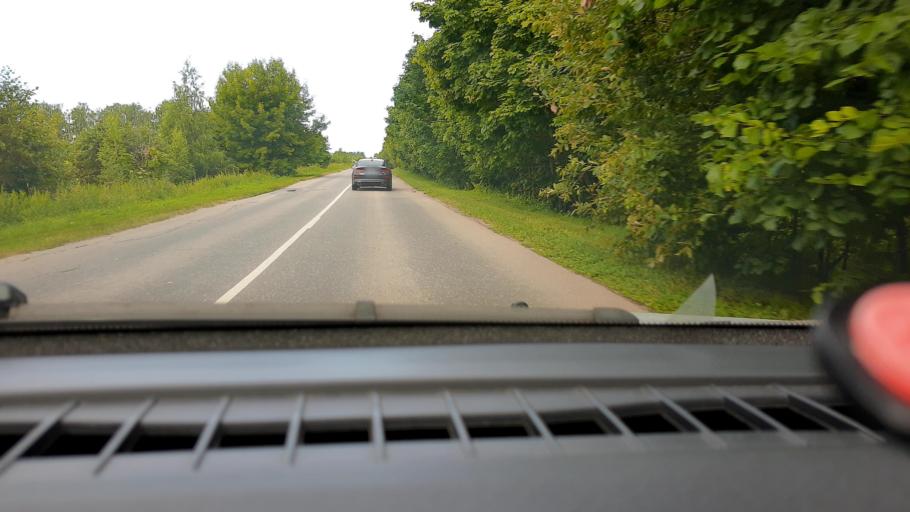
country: RU
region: Nizjnij Novgorod
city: Kstovo
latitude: 56.1486
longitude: 44.3145
